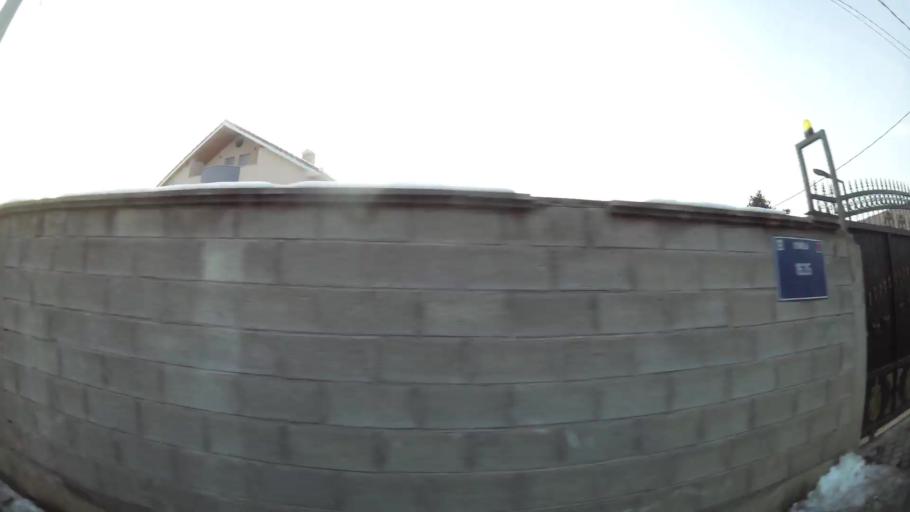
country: MK
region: Aracinovo
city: Arachinovo
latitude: 42.0147
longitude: 21.5260
